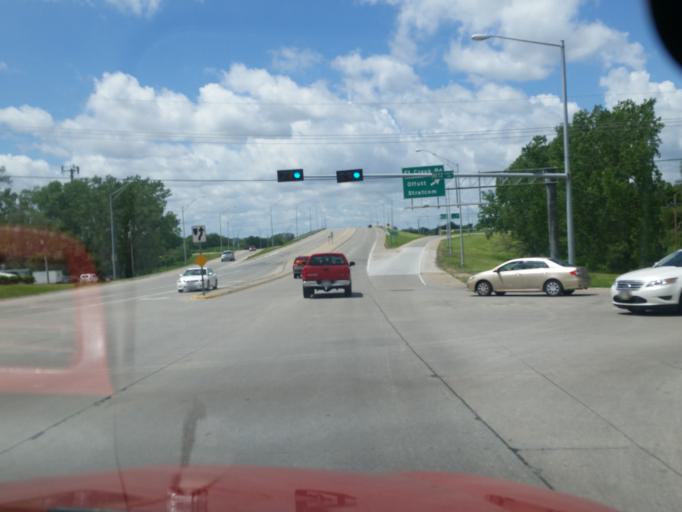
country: US
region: Nebraska
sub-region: Sarpy County
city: Offutt Air Force Base
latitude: 41.1403
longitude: -95.9216
